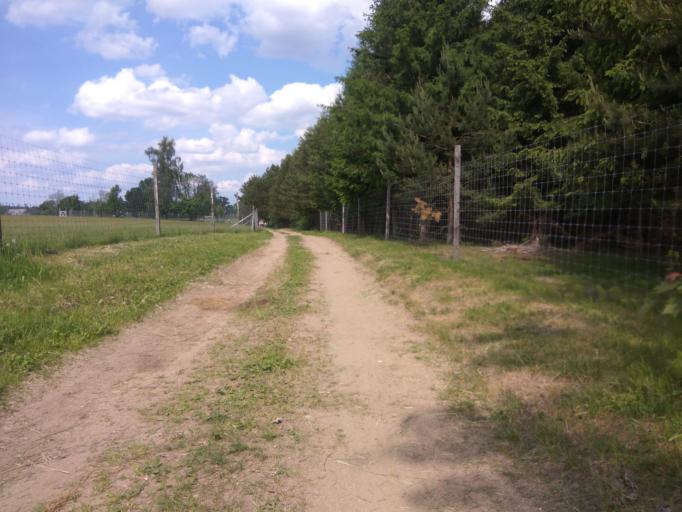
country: LV
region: Kuldigas Rajons
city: Kuldiga
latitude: 56.8877
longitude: 21.9300
